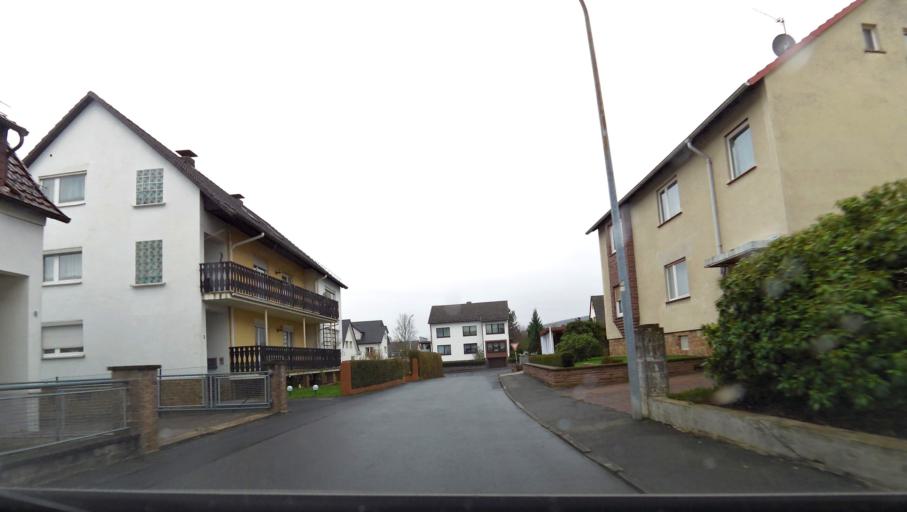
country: DE
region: Lower Saxony
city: Buhren
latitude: 51.4952
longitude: 9.5945
